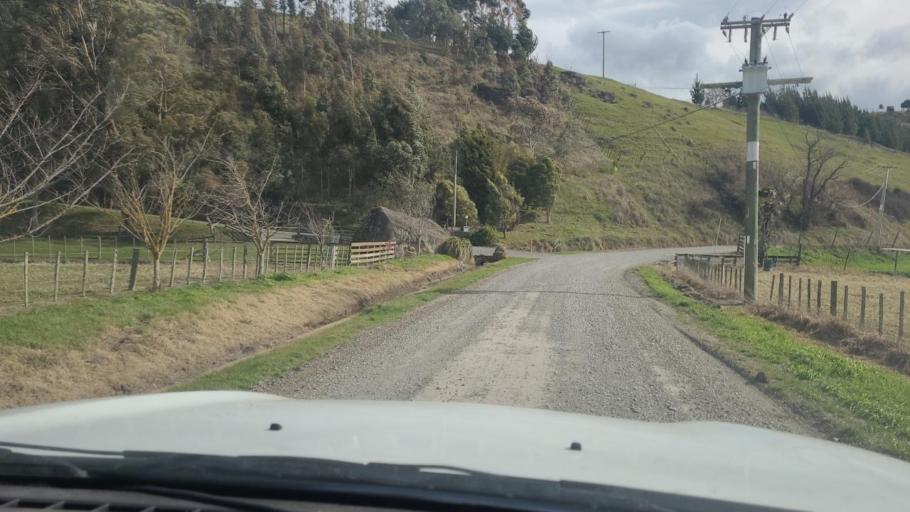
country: NZ
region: Hawke's Bay
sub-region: Napier City
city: Taradale
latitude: -39.5633
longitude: 176.7611
